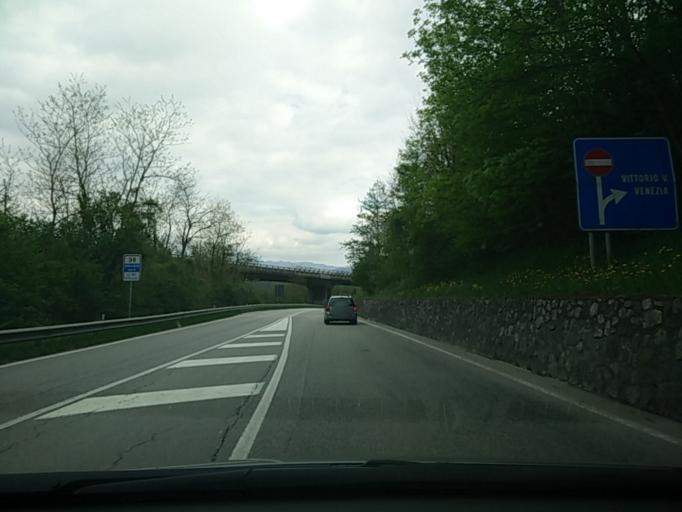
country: IT
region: Veneto
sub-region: Provincia di Belluno
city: Soccher-Paiane-Casan-Arsie
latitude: 46.1713
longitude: 12.3077
